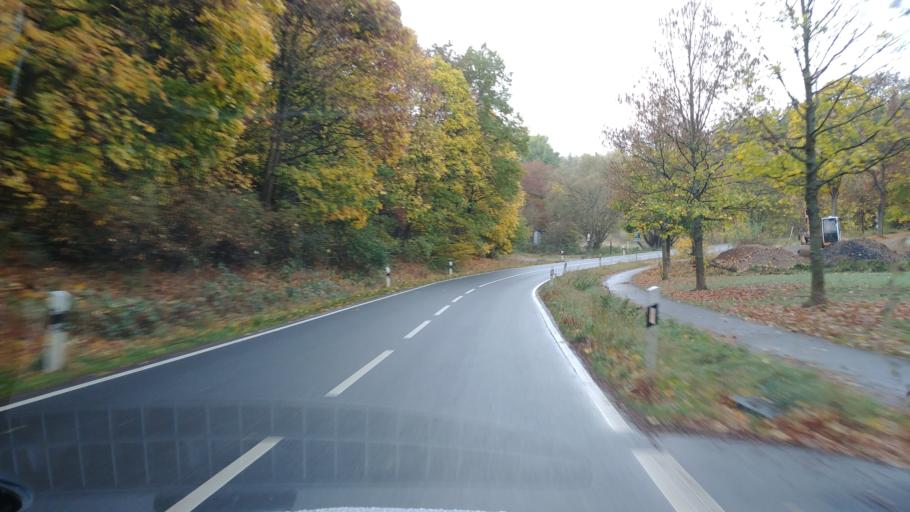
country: DE
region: Hesse
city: Taunusstein
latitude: 50.1343
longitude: 8.1331
